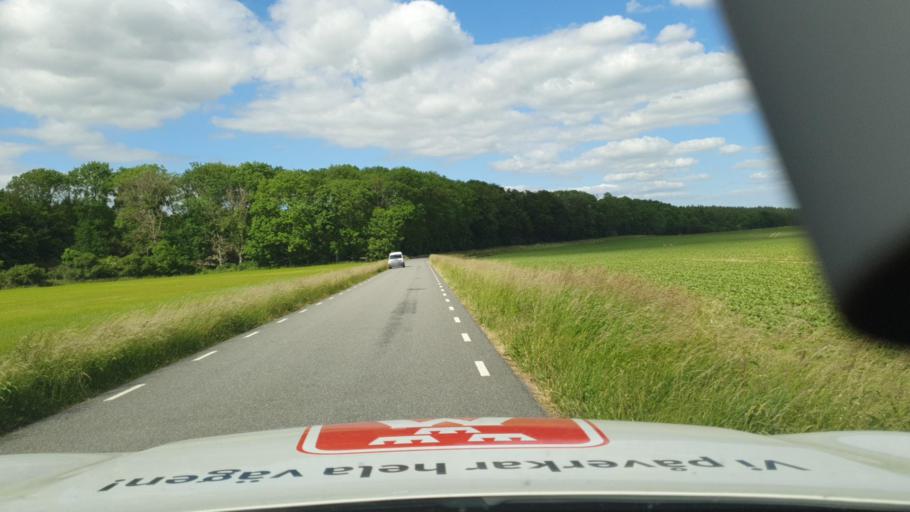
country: SE
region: Skane
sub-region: Ystads Kommun
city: Kopingebro
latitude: 55.4750
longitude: 13.9997
